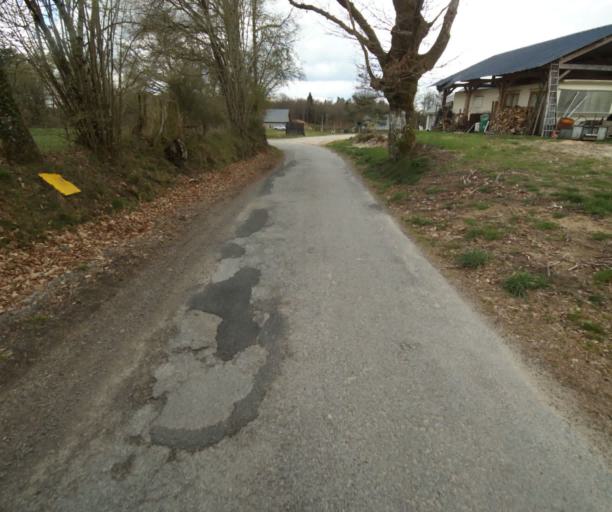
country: FR
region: Limousin
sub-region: Departement de la Correze
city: Correze
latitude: 45.2962
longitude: 1.9216
